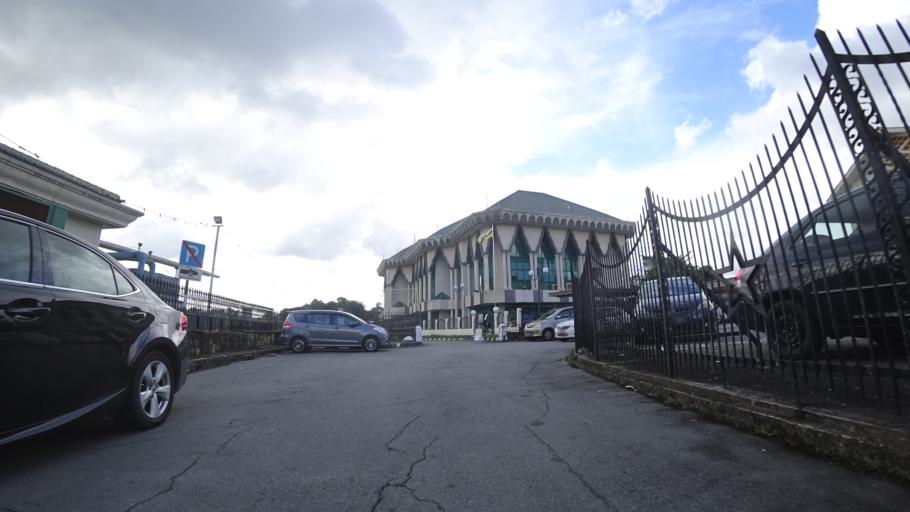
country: BN
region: Brunei and Muara
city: Bandar Seri Begawan
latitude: 4.8903
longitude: 114.9390
